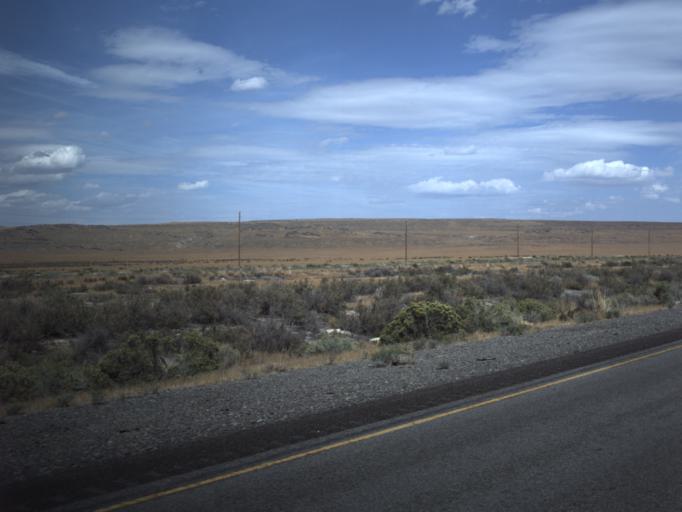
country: US
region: Utah
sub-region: Tooele County
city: Grantsville
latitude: 40.7485
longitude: -113.0520
